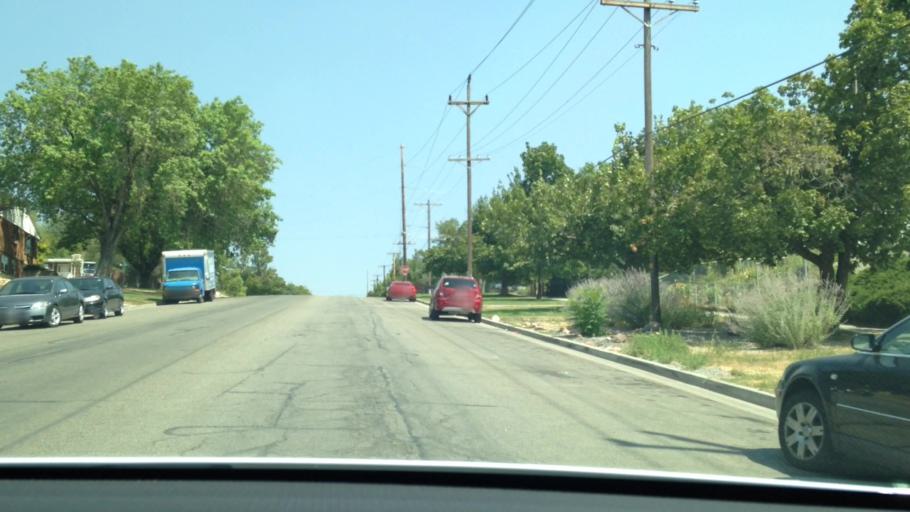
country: US
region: Utah
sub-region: Salt Lake County
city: Salt Lake City
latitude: 40.7563
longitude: -111.8638
